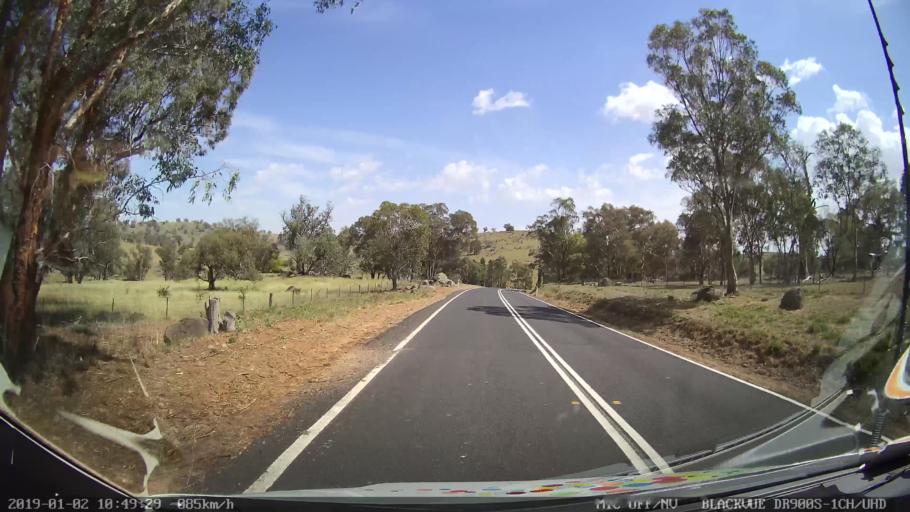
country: AU
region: New South Wales
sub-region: Cootamundra
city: Cootamundra
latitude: -34.7240
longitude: 148.2763
